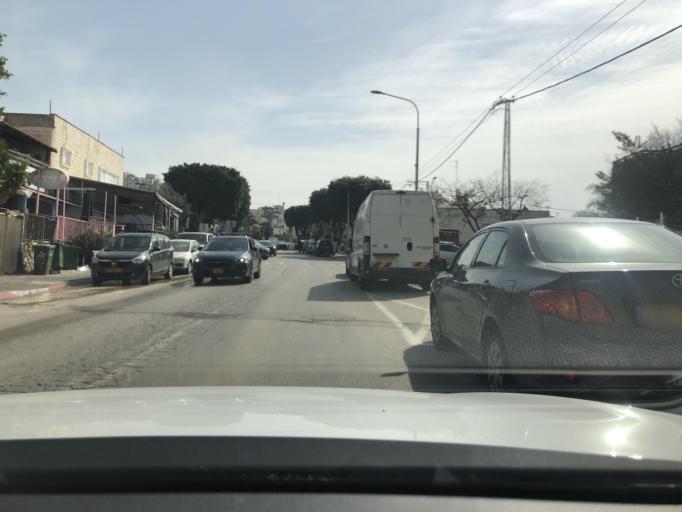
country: IL
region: Central District
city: Rosh Ha'Ayin
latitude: 32.0884
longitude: 34.9515
